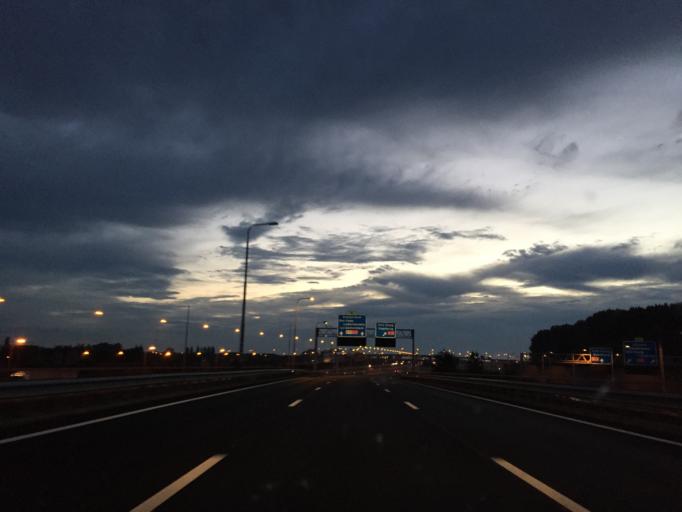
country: NL
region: South Holland
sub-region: Gemeente Den Haag
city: Ypenburg
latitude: 52.0543
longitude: 4.3677
